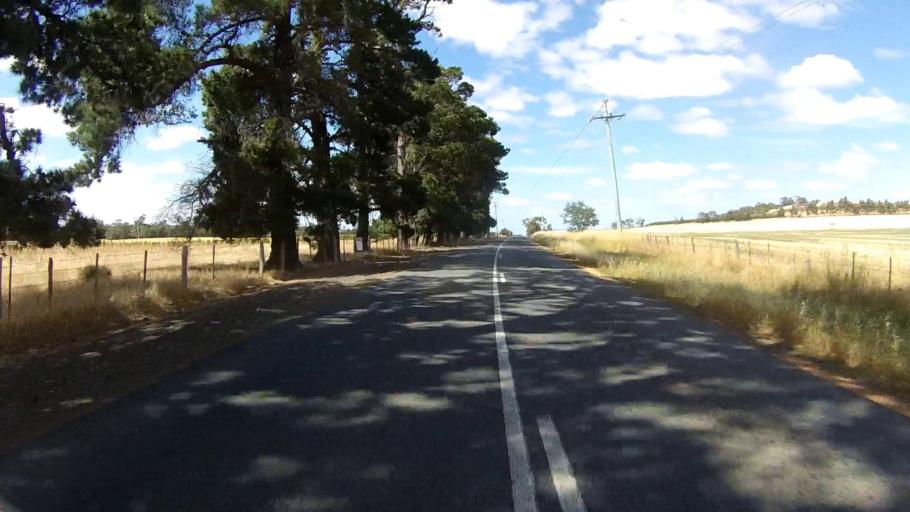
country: AU
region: Tasmania
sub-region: Sorell
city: Sorell
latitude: -42.6392
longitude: 147.4331
